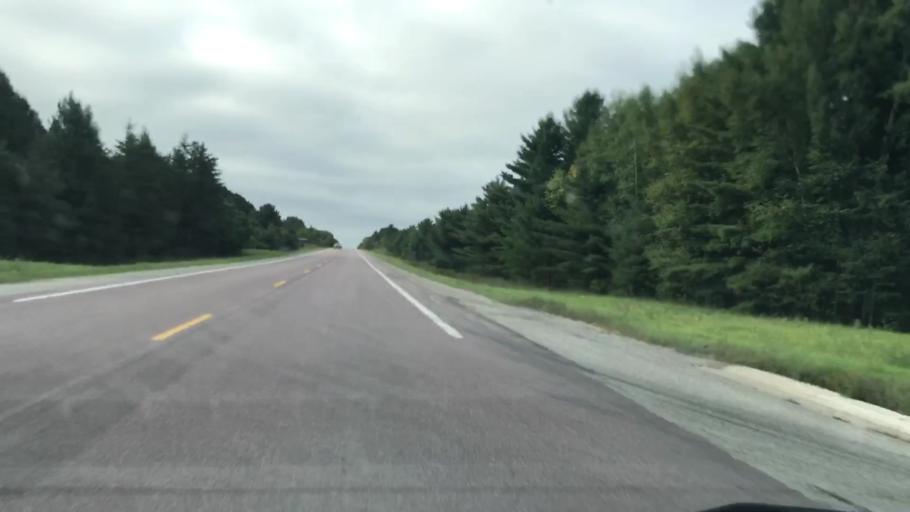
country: US
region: Michigan
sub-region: Luce County
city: Newberry
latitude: 46.2887
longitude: -85.5701
